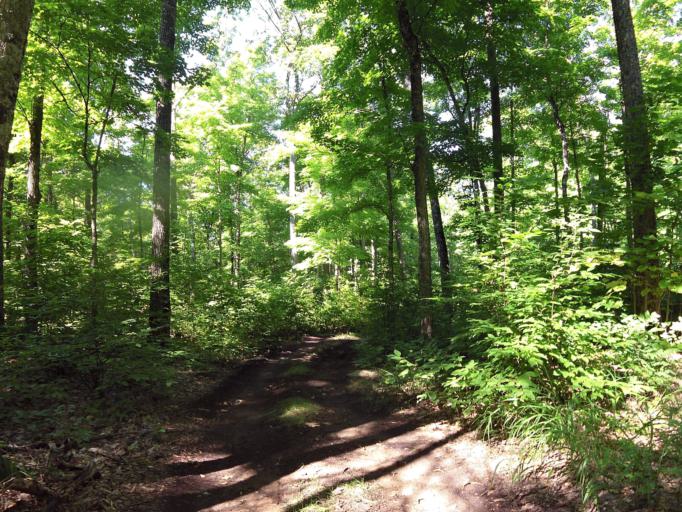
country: CA
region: Ontario
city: Renfrew
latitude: 45.1296
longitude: -76.7335
